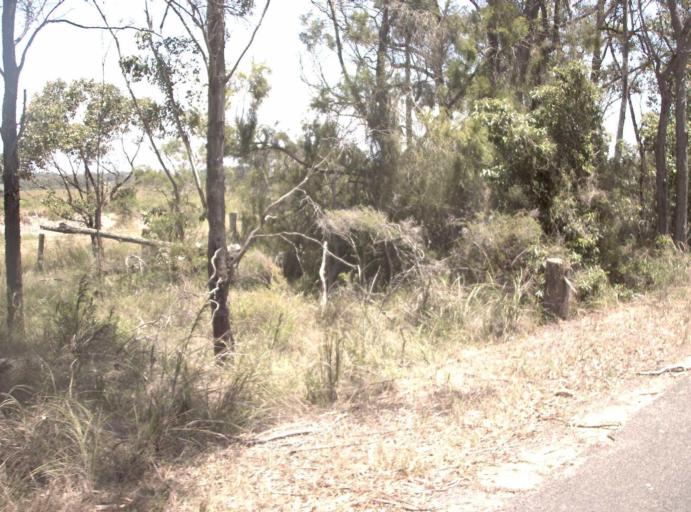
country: AU
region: Victoria
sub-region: East Gippsland
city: Lakes Entrance
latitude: -37.8400
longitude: 148.0349
